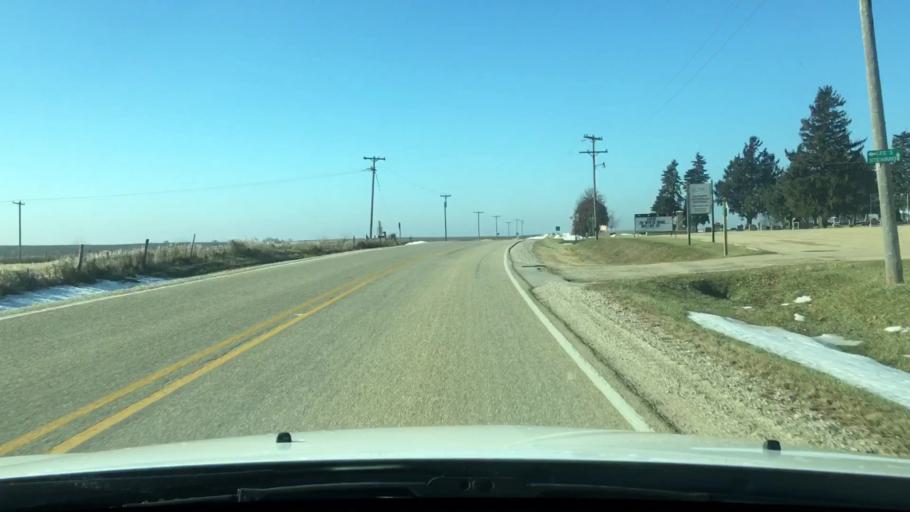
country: US
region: Illinois
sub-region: DeKalb County
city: Malta
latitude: 41.8482
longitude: -88.9401
